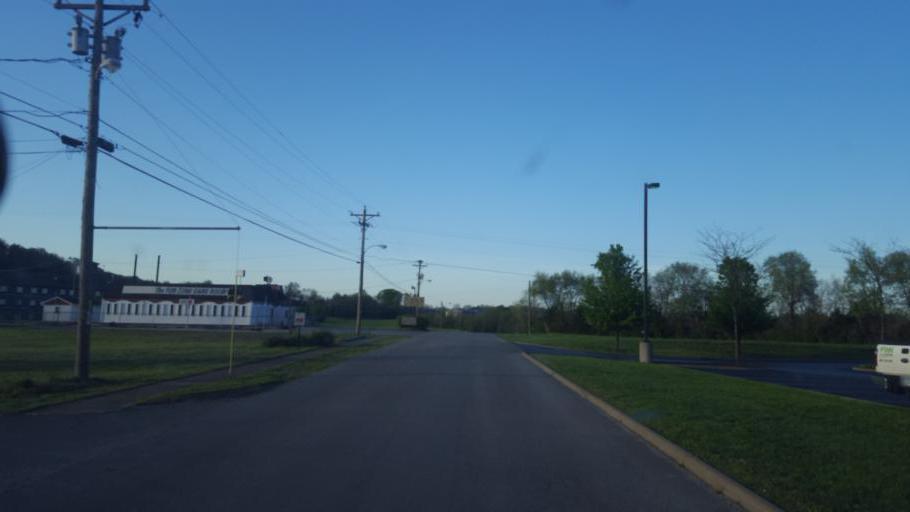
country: US
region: Kentucky
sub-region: Barren County
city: Cave City
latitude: 37.1353
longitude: -85.9716
